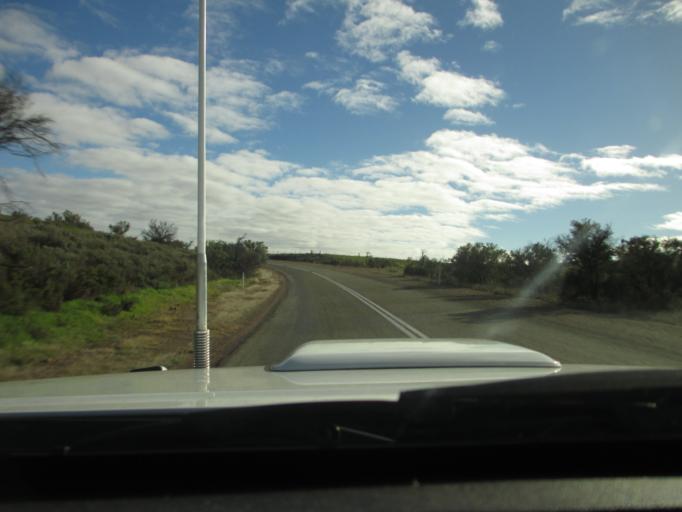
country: AU
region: South Australia
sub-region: Peterborough
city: Peterborough
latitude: -32.6372
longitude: 138.5981
